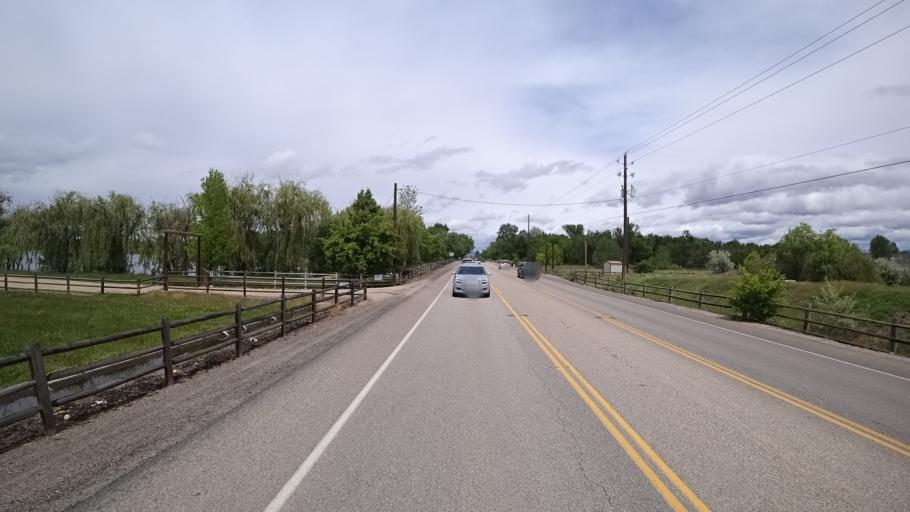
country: US
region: Idaho
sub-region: Ada County
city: Eagle
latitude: 43.6853
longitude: -116.4138
